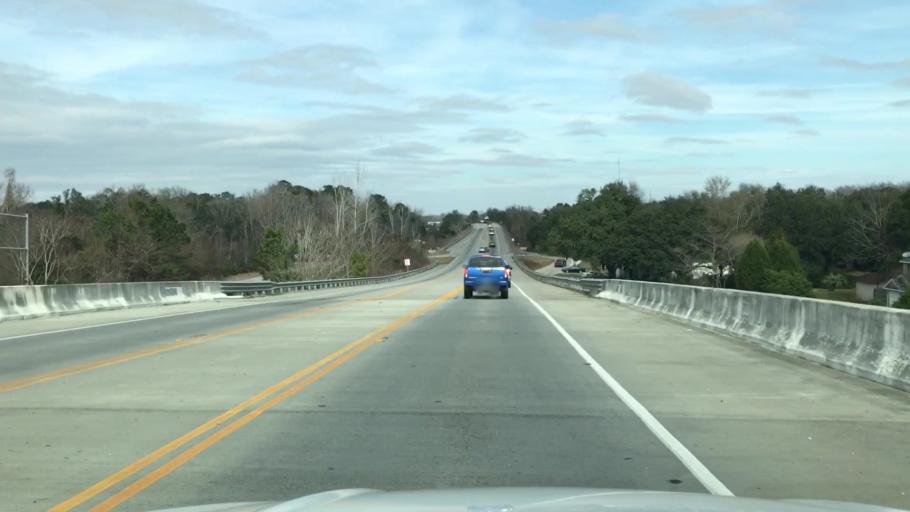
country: US
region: South Carolina
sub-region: Charleston County
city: Shell Point
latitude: 32.7886
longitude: -80.1080
